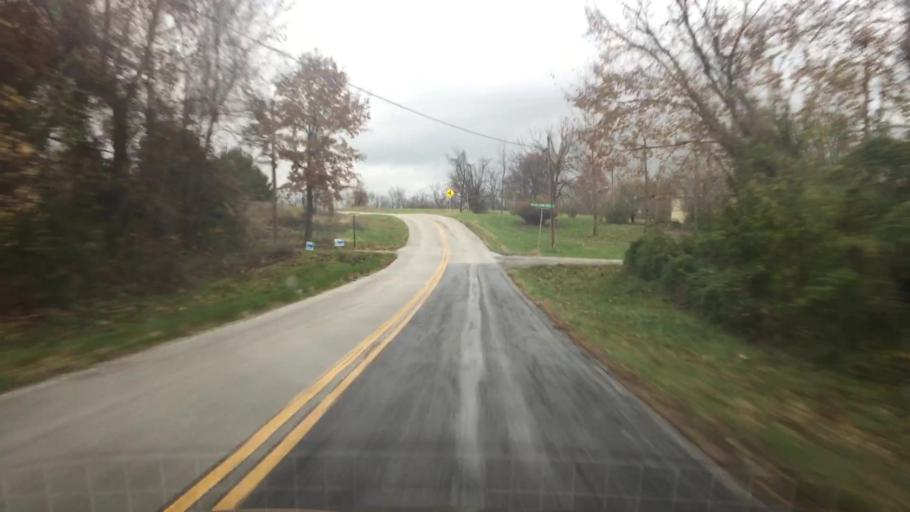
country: US
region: Missouri
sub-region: Boone County
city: Columbia
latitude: 38.9142
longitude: -92.4691
